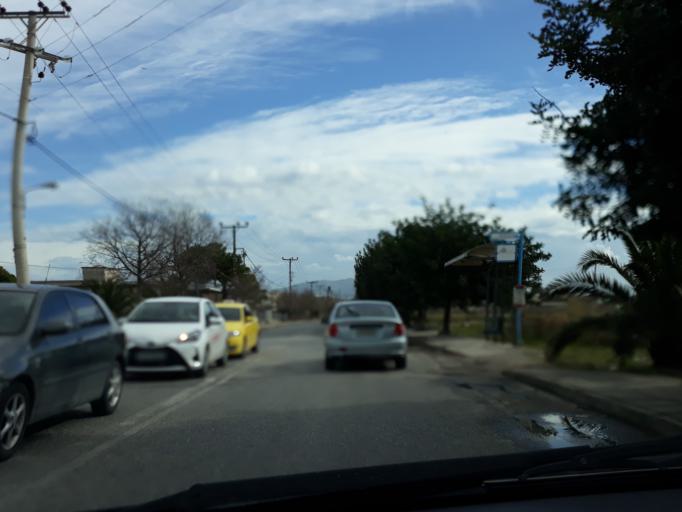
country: GR
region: Attica
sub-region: Nomarchia Dytikis Attikis
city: Ano Liosia
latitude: 38.0797
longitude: 23.7102
